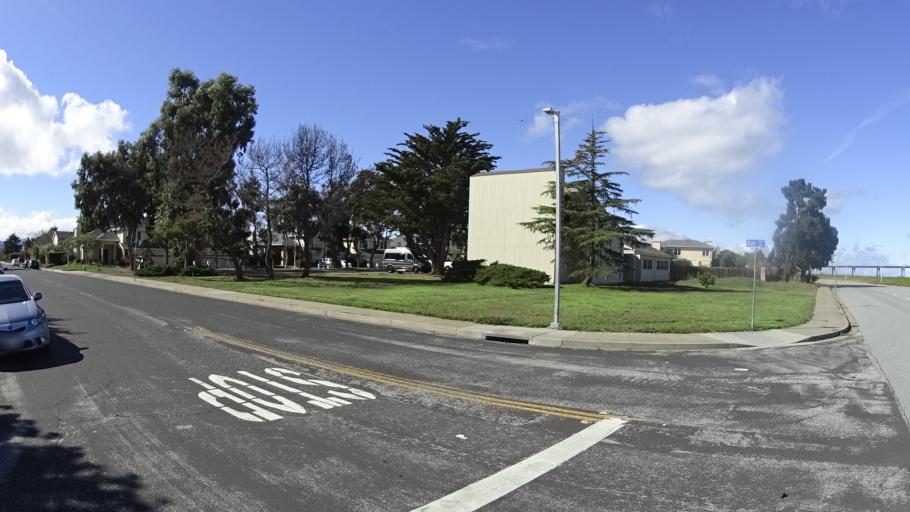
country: US
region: California
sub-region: San Mateo County
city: Foster City
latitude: 37.5660
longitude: -122.2514
